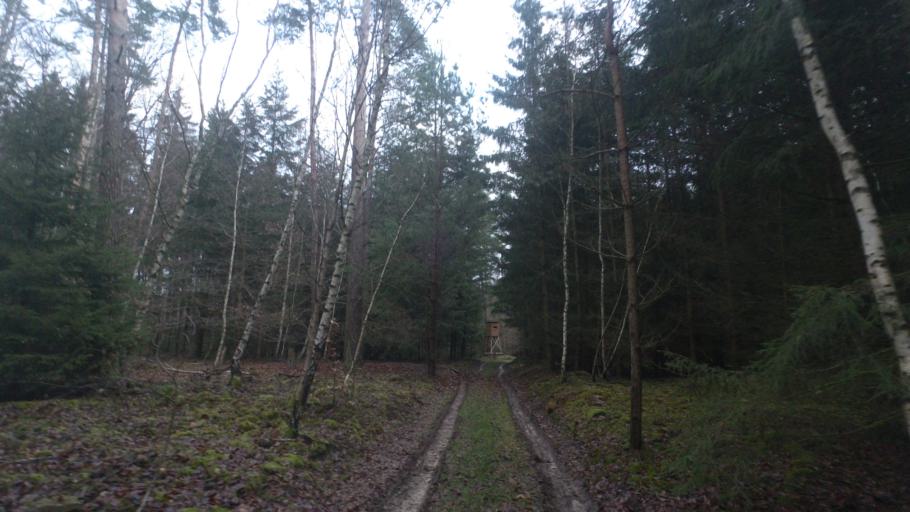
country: DE
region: Thuringia
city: Herschdorf
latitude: 50.7050
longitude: 11.4863
